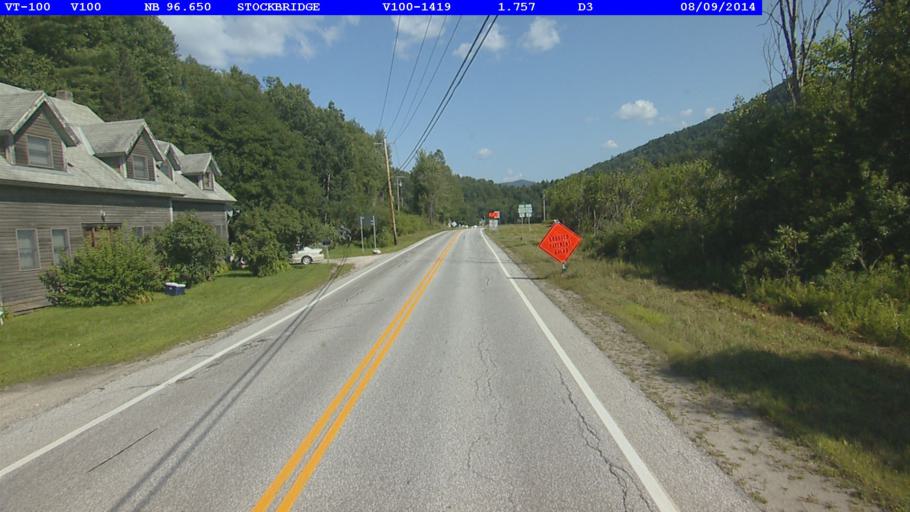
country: US
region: Vermont
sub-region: Orange County
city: Randolph
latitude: 43.7755
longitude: -72.7649
